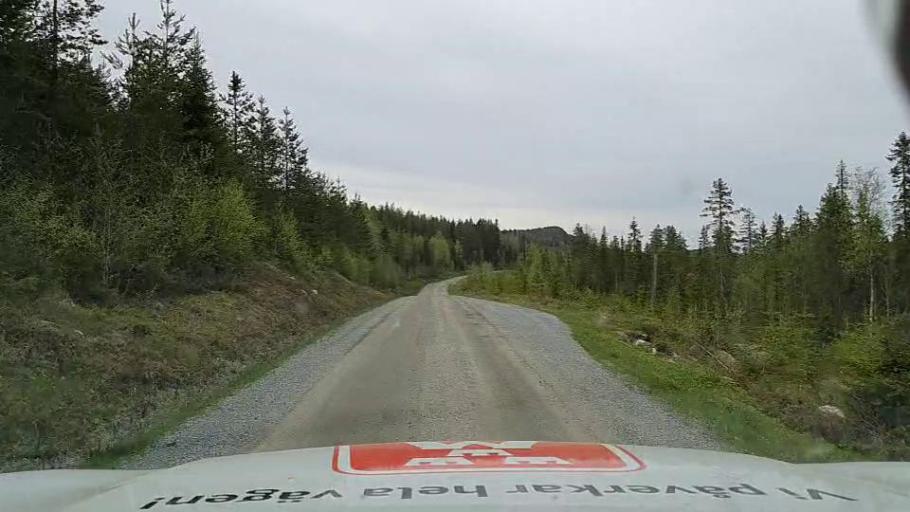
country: SE
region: Jaemtland
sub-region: Bergs Kommun
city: Hoverberg
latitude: 62.5441
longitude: 14.9003
